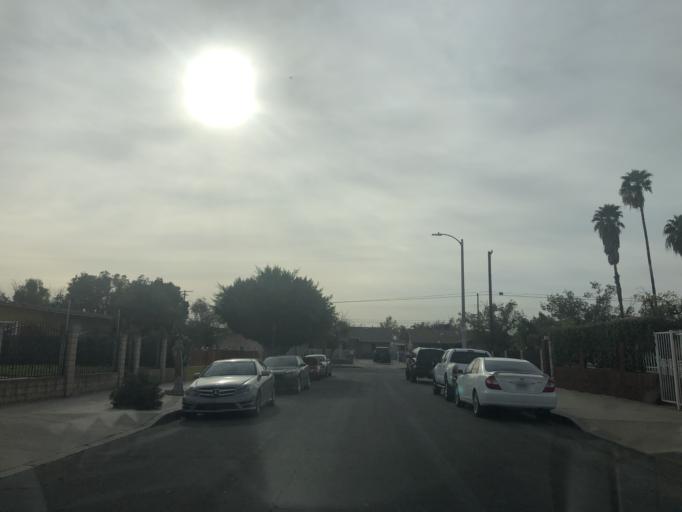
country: US
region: California
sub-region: Los Angeles County
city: San Fernando
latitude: 34.2696
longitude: -118.4353
